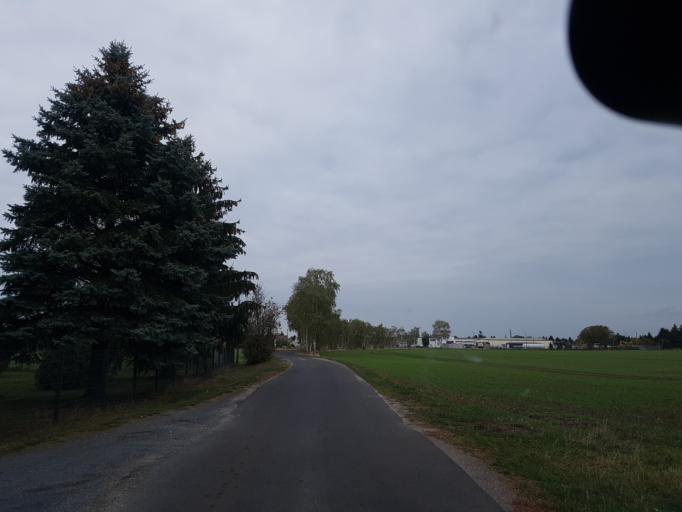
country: DE
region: Brandenburg
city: Finsterwalde
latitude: 51.6186
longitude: 13.6929
